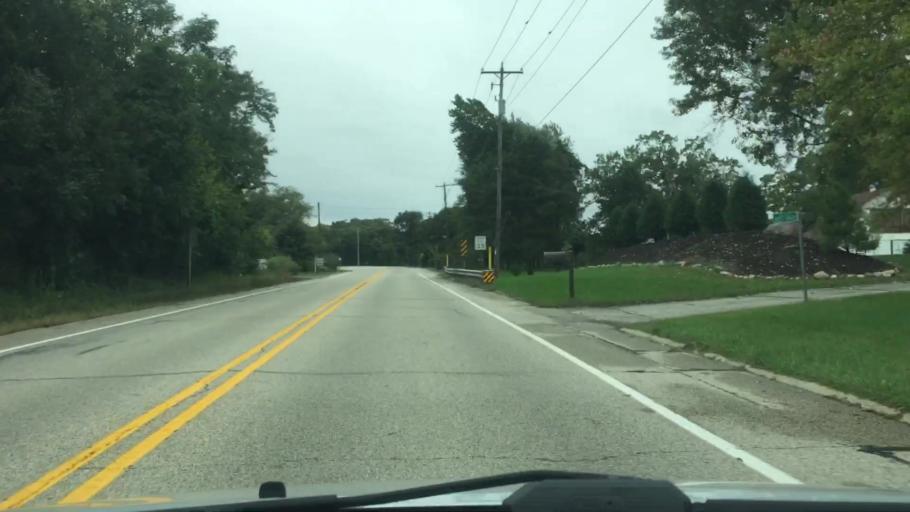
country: US
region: Wisconsin
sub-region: Waukesha County
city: Eagle
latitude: 42.8699
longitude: -88.4848
